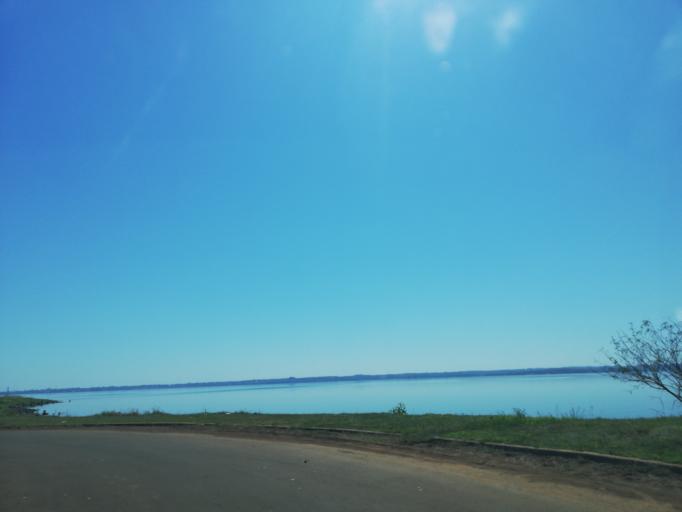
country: AR
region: Misiones
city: Garupa
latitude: -27.4332
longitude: -55.8624
